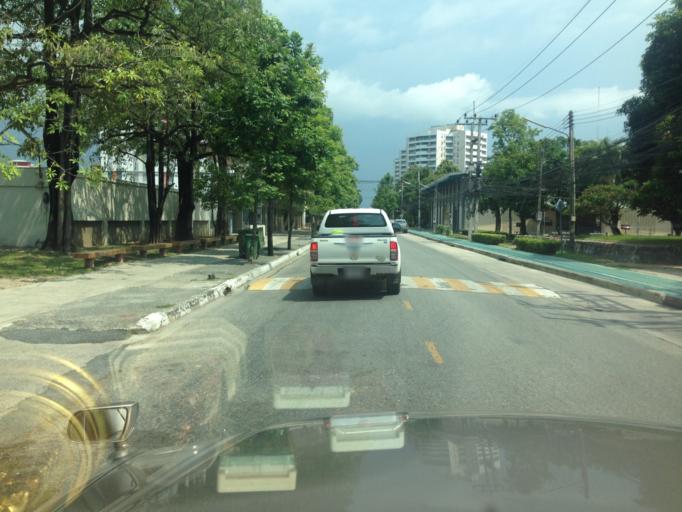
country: TH
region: Chon Buri
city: Si Racha
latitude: 13.2760
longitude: 100.9282
